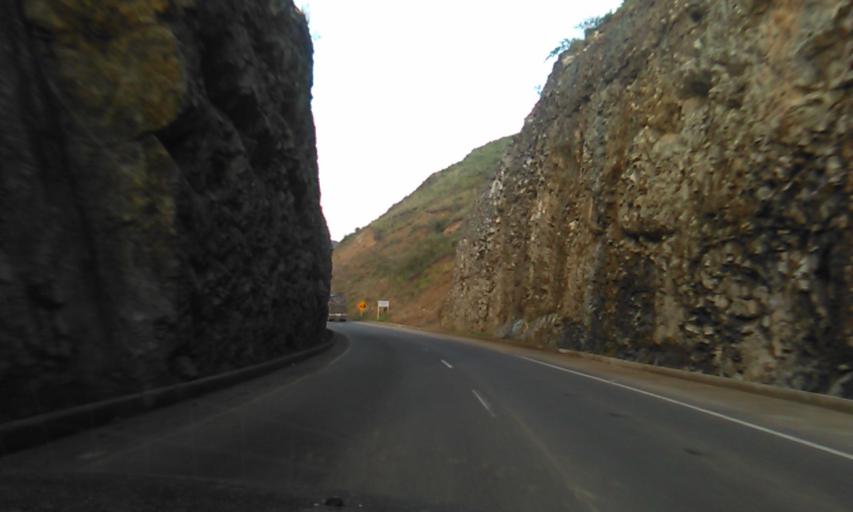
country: CO
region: Valle del Cauca
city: Yotoco
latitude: 3.8908
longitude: -76.3912
